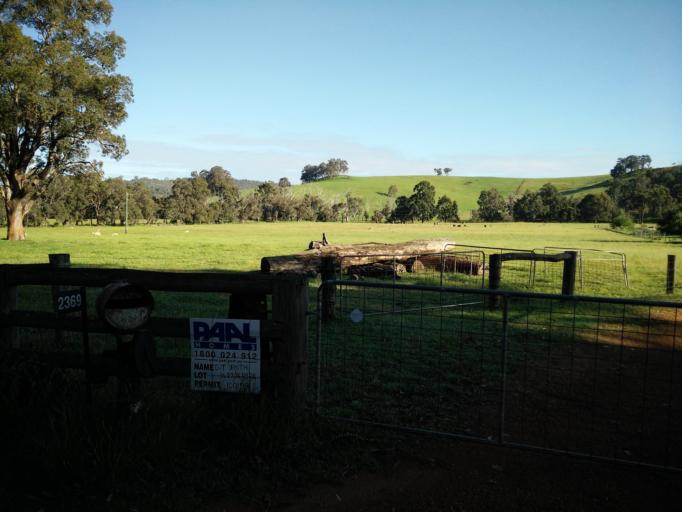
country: AU
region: Western Australia
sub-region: Collie
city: Collie
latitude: -33.5298
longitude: 116.0719
